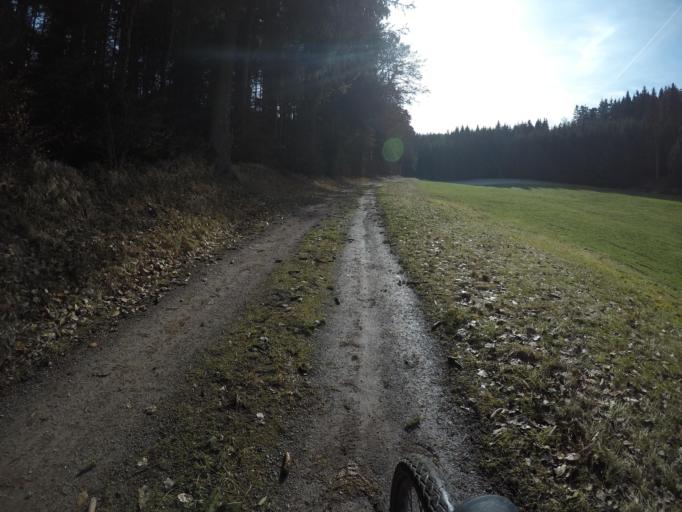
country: DE
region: Baden-Wuerttemberg
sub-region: Regierungsbezirk Stuttgart
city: Oberjettingen
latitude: 48.5989
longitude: 8.7901
